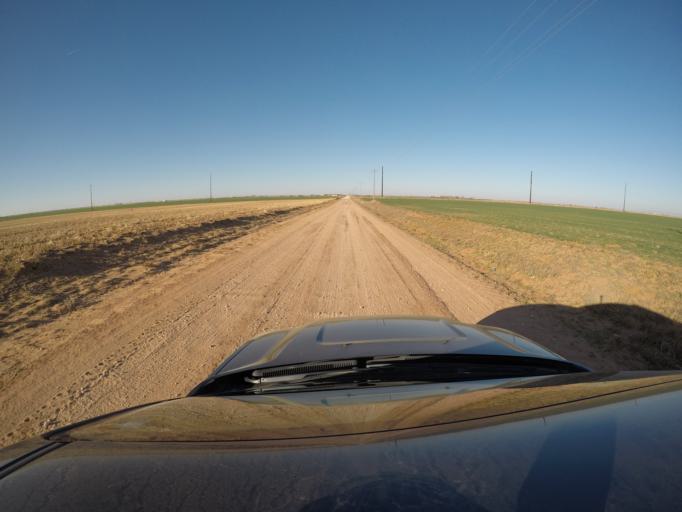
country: US
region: New Mexico
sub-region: Curry County
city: Texico
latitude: 34.3587
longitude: -103.1083
